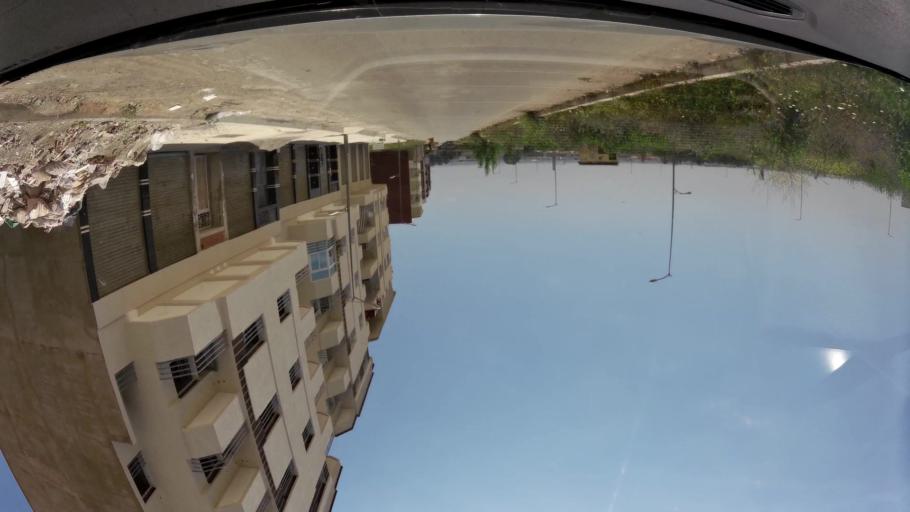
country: MA
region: Fes-Boulemane
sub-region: Fes
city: Fes
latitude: 34.0510
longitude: -5.0409
